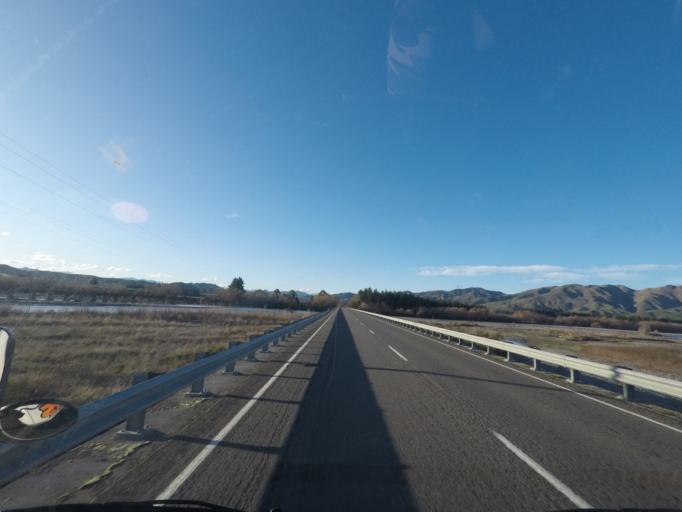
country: NZ
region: Canterbury
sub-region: Kaikoura District
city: Kaikoura
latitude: -42.7230
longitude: 173.2829
